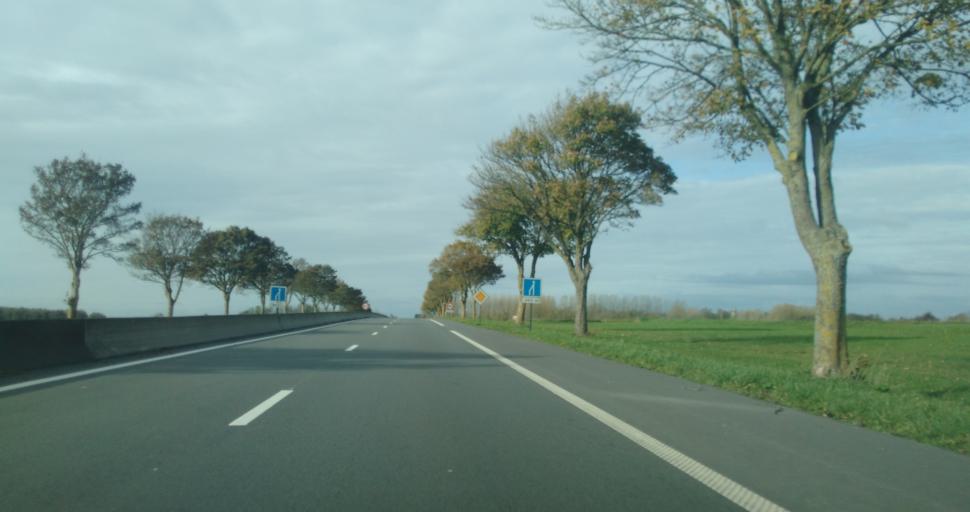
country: FR
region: Nord-Pas-de-Calais
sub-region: Departement du Pas-de-Calais
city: Saint-Pol-sur-Ternoise
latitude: 50.3782
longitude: 2.2908
